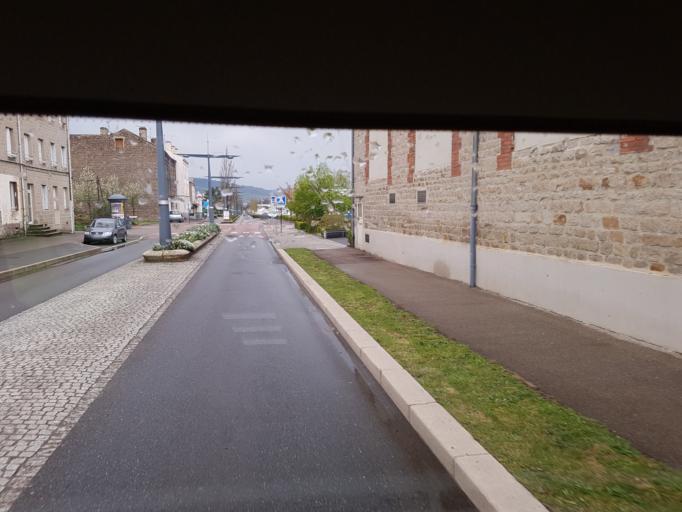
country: FR
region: Rhone-Alpes
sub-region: Departement de la Loire
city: Le Chambon-Feugerolles
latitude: 45.3953
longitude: 4.3146
